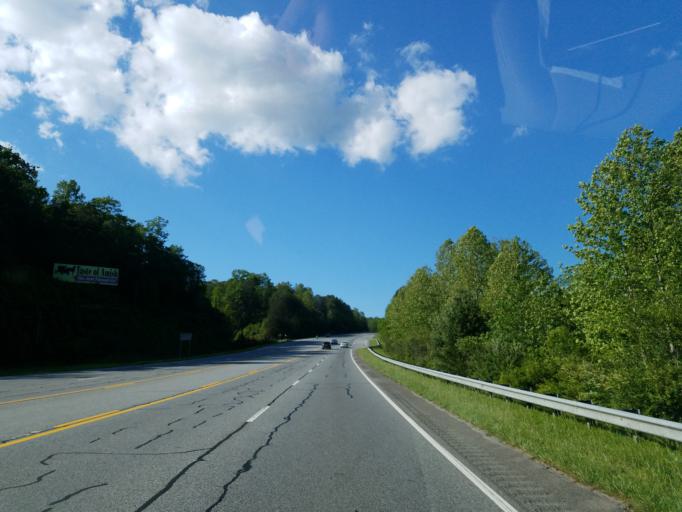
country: US
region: Georgia
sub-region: Fannin County
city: Blue Ridge
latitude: 34.8536
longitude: -84.3370
